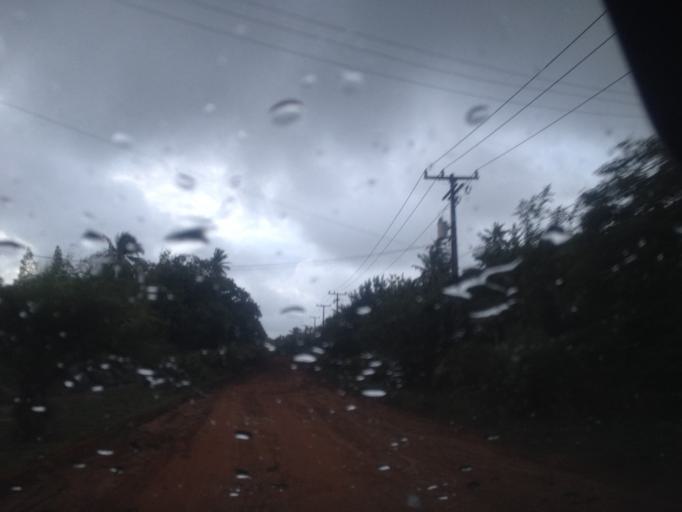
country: BR
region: Bahia
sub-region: Mata De Sao Joao
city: Mata de Sao Joao
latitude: -12.5740
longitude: -38.0260
